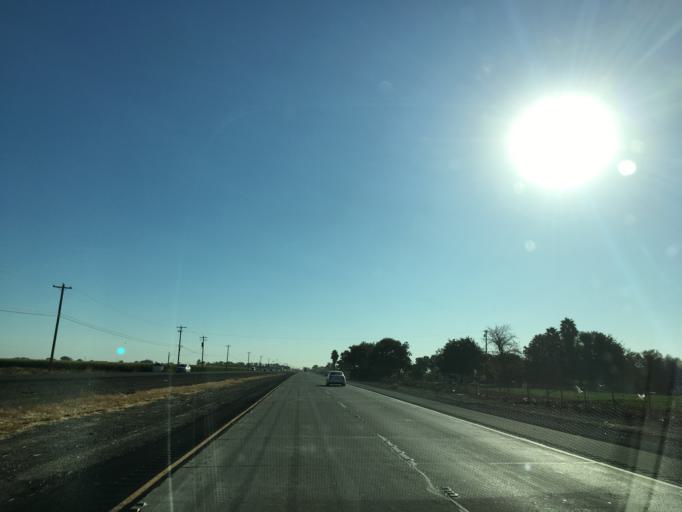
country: US
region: California
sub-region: Merced County
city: Los Banos
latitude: 37.0566
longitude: -120.9107
